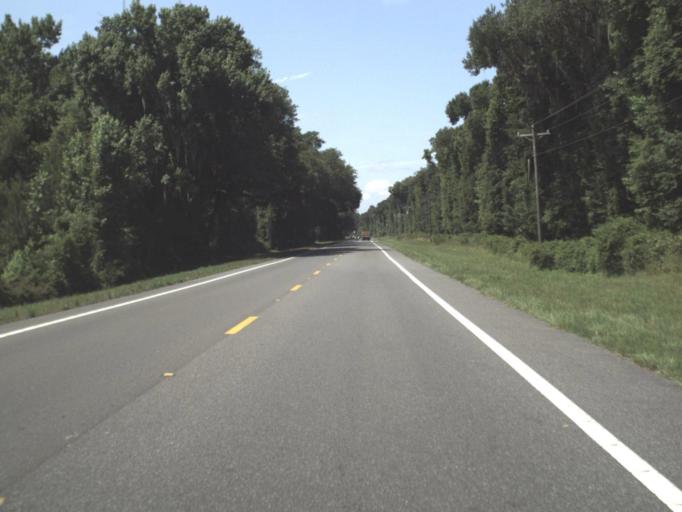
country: US
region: Florida
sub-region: Alachua County
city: Archer
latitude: 29.5461
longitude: -82.3966
